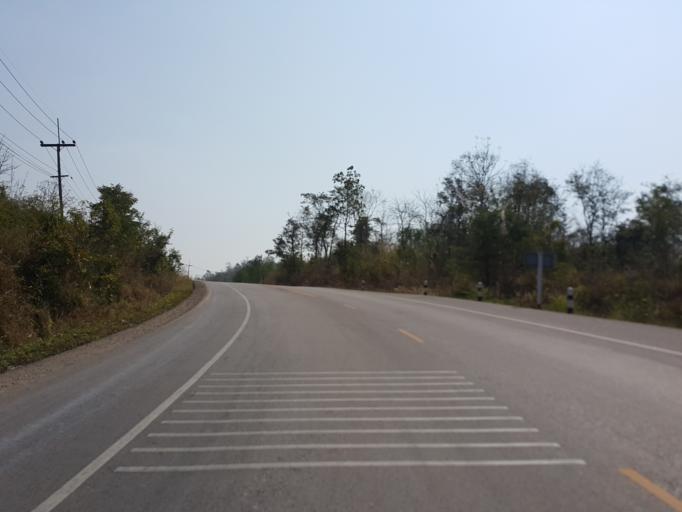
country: TH
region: Lampang
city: Mueang Pan
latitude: 18.8852
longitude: 99.6026
